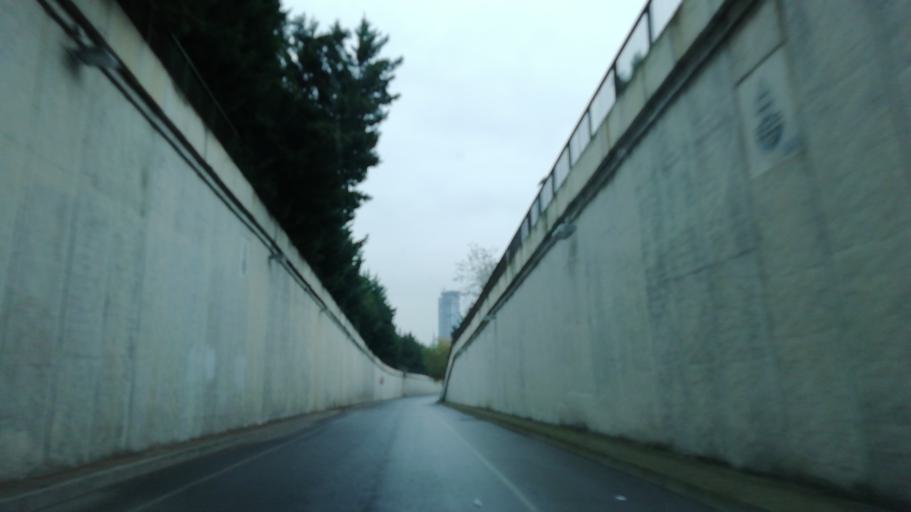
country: TR
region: Istanbul
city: UEskuedar
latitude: 41.0146
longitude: 29.0564
